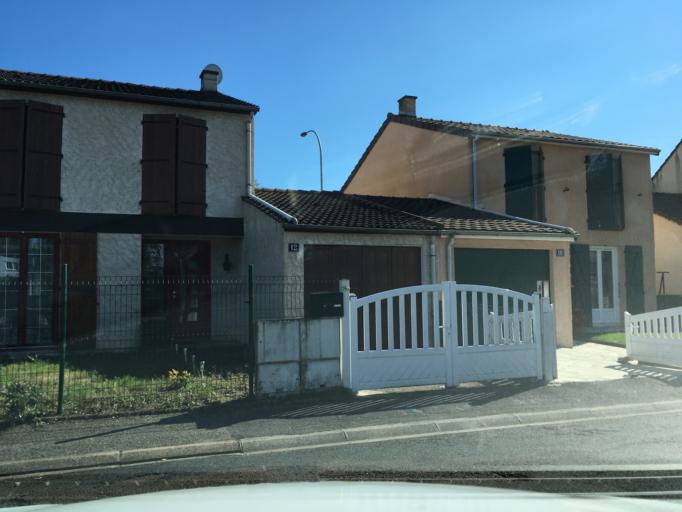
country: FR
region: Limousin
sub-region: Departement de la Correze
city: Brive-la-Gaillarde
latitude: 45.1592
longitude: 1.4958
